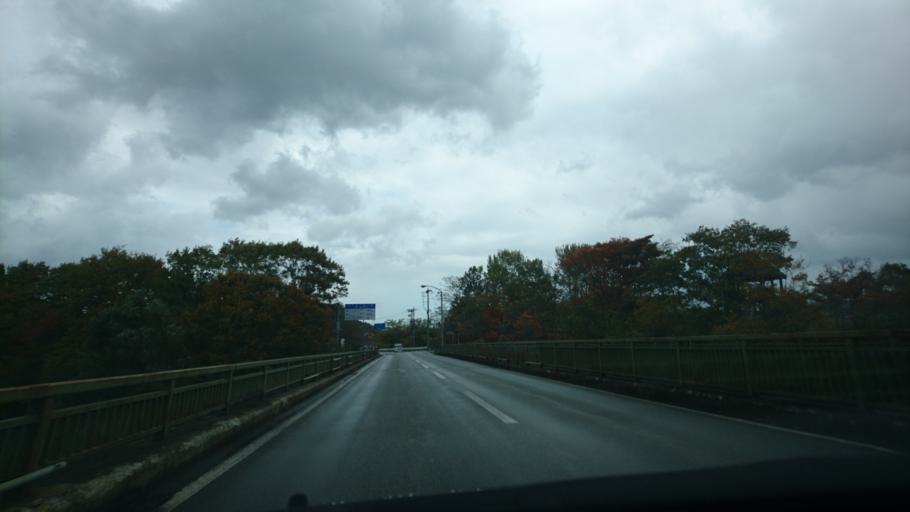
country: JP
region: Iwate
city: Shizukuishi
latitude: 39.6754
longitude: 140.9910
